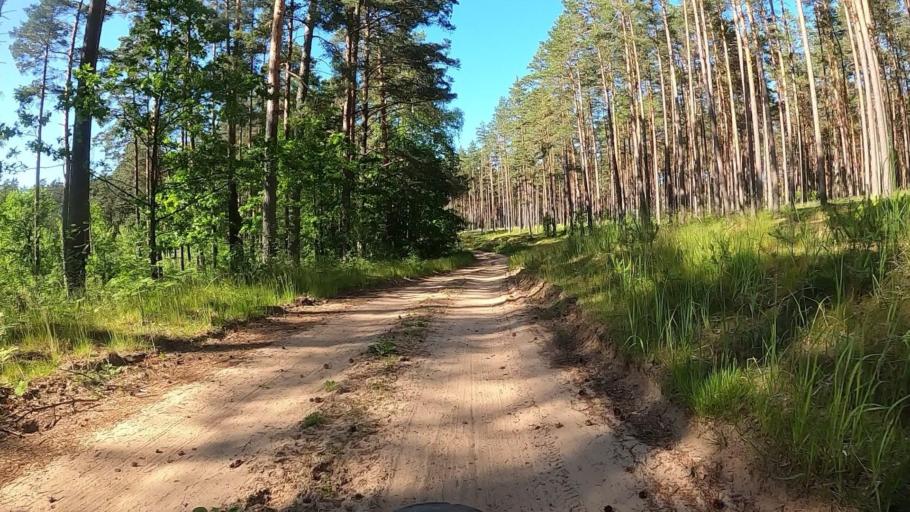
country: LV
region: Riga
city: Bergi
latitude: 57.0347
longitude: 24.2477
